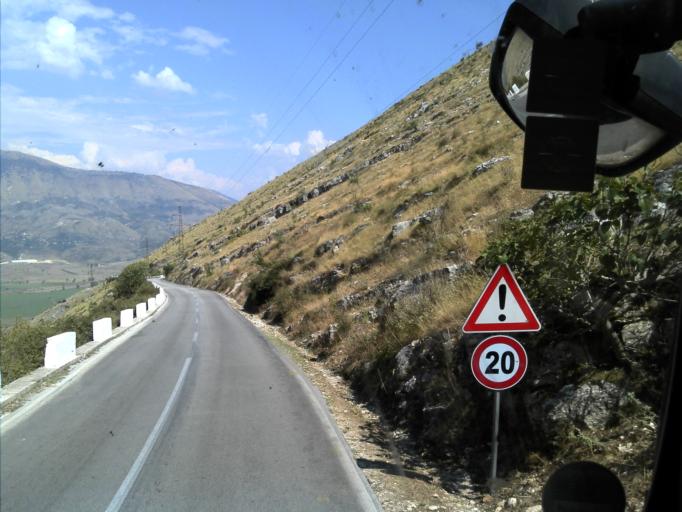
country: AL
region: Gjirokaster
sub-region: Rrethi i Gjirokastres
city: Libohove
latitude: 39.9445
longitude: 20.2337
